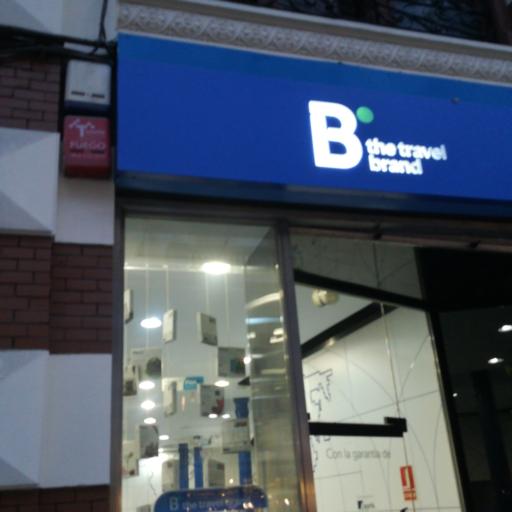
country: ES
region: Valencia
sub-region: Provincia de Valencia
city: Valencia
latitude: 39.4731
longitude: -0.3718
